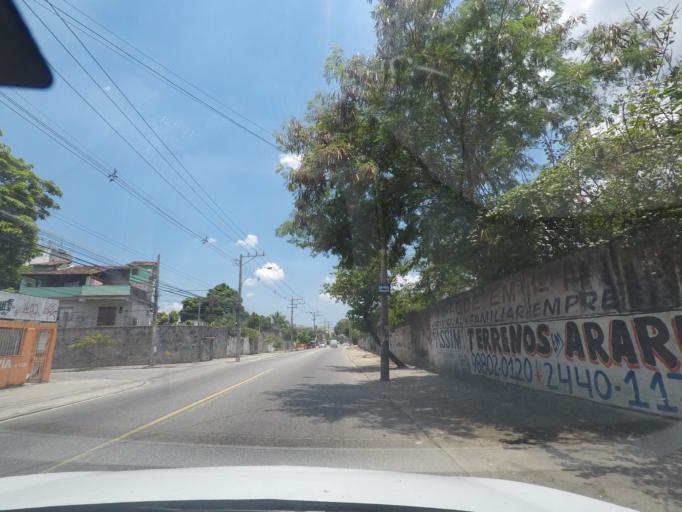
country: BR
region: Rio de Janeiro
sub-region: Sao Joao De Meriti
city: Sao Joao de Meriti
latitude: -22.8654
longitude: -43.3562
